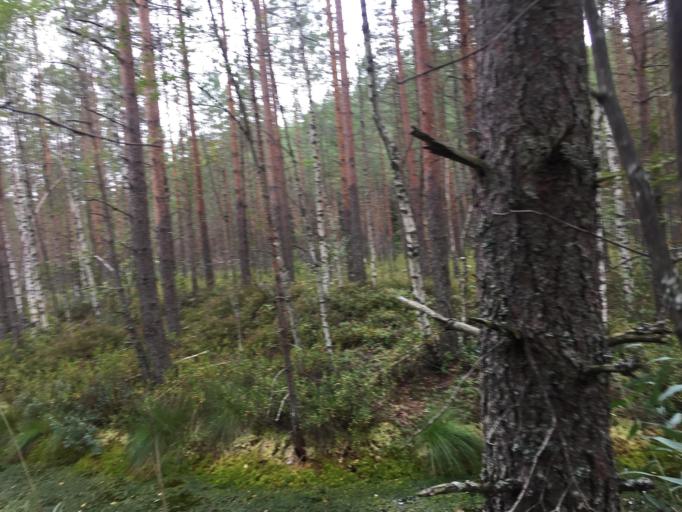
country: RU
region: Leningrad
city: Rozhdestveno
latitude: 59.2911
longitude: 30.0079
